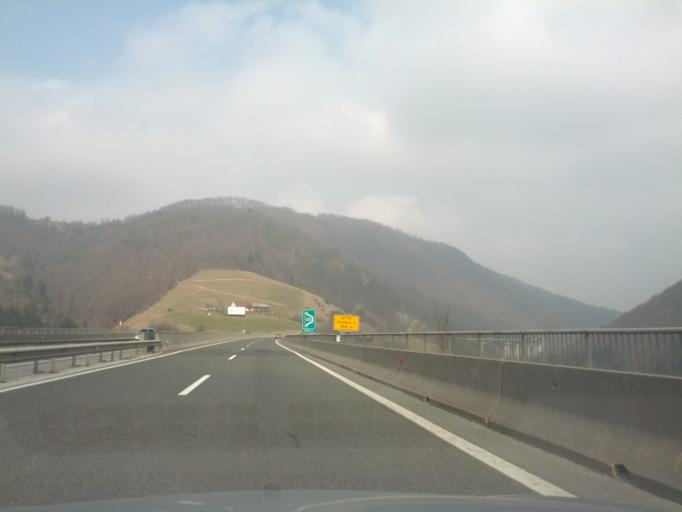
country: SI
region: Slovenska Konjice
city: Slovenske Konjice
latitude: 46.3015
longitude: 15.4447
